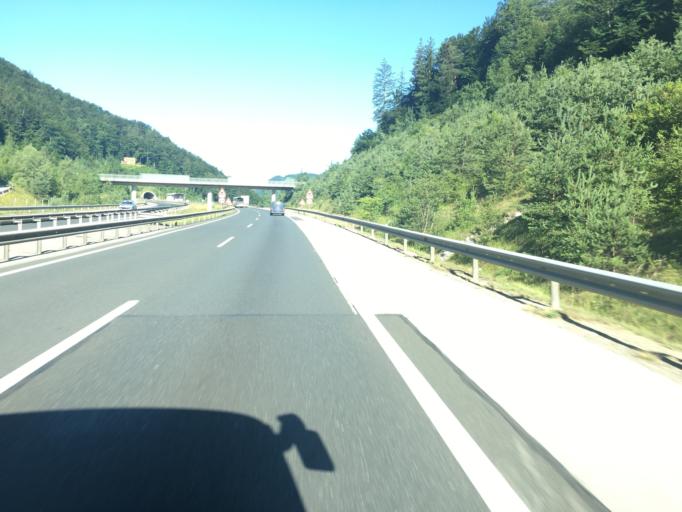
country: SI
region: Vransko
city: Vransko
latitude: 46.2180
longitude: 14.9236
